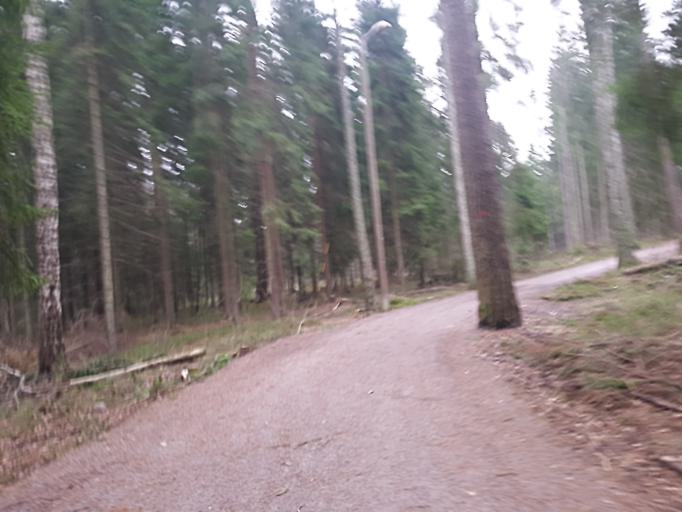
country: FI
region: Uusimaa
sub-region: Helsinki
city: Helsinki
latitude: 60.2257
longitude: 24.9174
